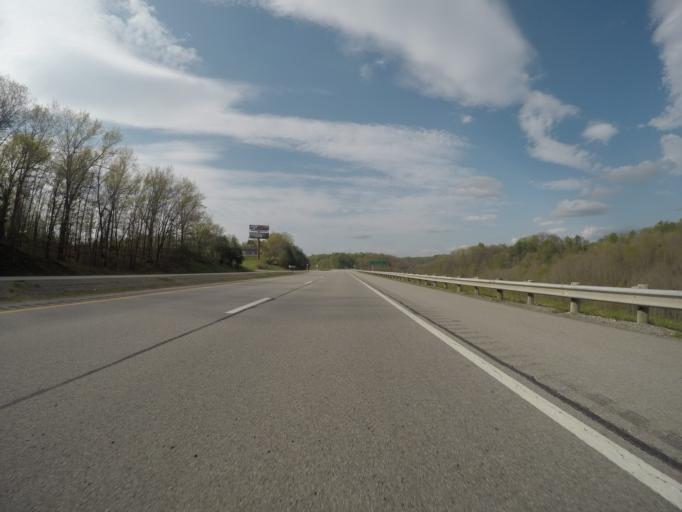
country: US
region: West Virginia
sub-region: Kanawha County
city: Alum Creek
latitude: 38.2408
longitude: -81.8389
